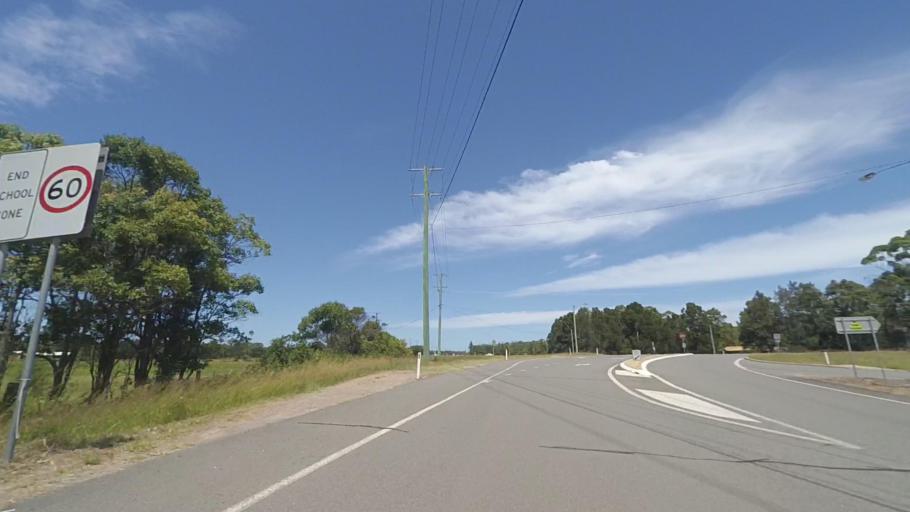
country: AU
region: New South Wales
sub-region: Port Stephens Shire
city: Anna Bay
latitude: -32.7663
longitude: 152.0125
